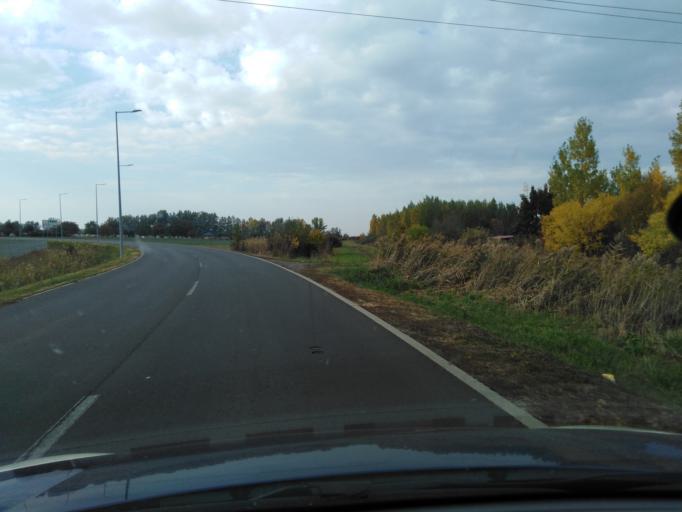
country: HU
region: Heves
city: Hatvan
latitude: 47.6781
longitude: 19.6631
